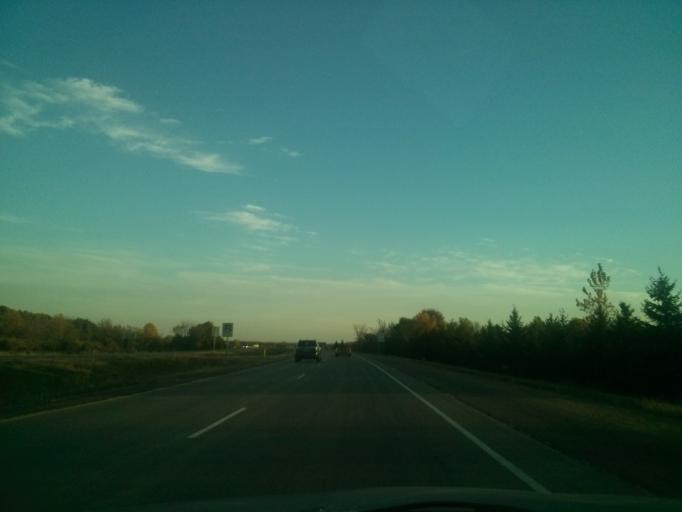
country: US
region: Wisconsin
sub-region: Saint Croix County
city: Hudson
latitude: 44.9398
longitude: -92.6934
